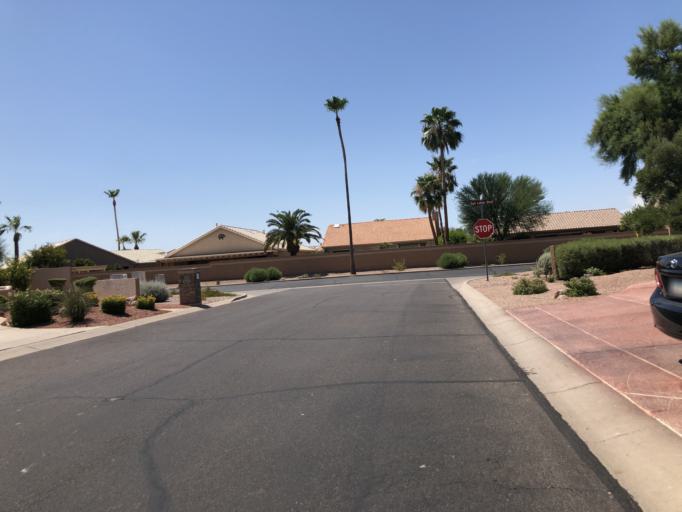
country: US
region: Arizona
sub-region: Maricopa County
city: Sun Lakes
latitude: 33.2289
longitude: -111.8803
